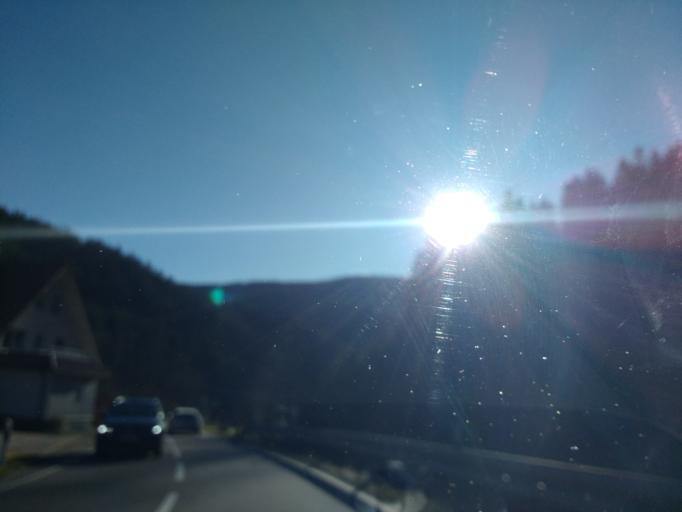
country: DE
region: Baden-Wuerttemberg
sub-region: Karlsruhe Region
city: Bad Rippoldsau-Schapbach
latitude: 48.4176
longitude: 8.3291
